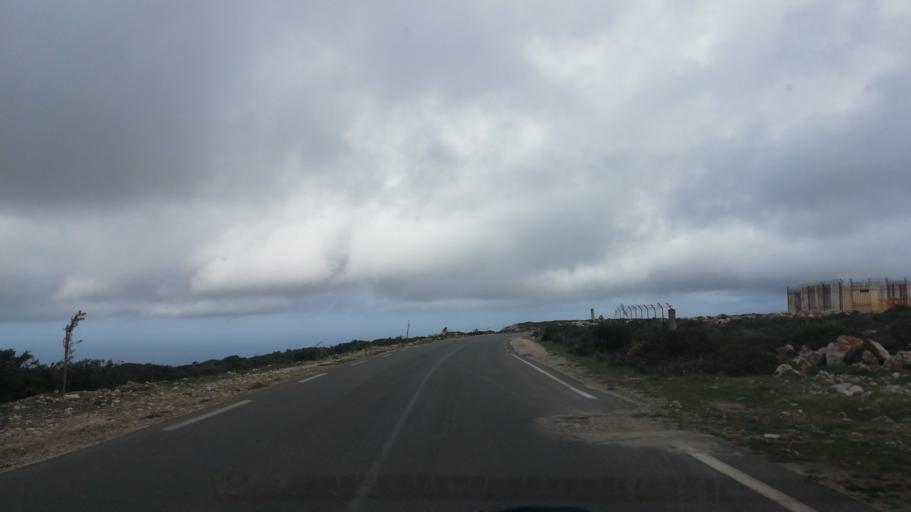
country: DZ
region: Oran
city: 'Ain el Turk
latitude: 35.6973
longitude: -0.7705
